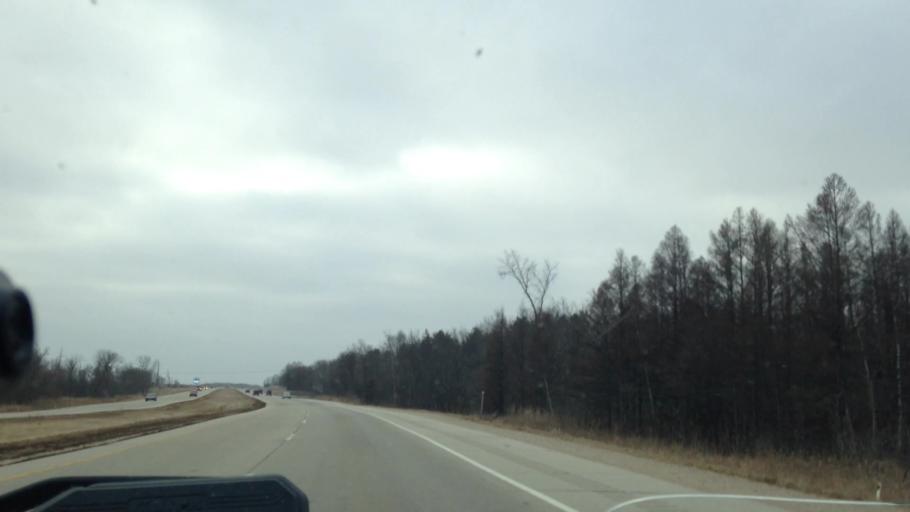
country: US
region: Wisconsin
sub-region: Washington County
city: Jackson
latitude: 43.3696
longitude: -88.1942
